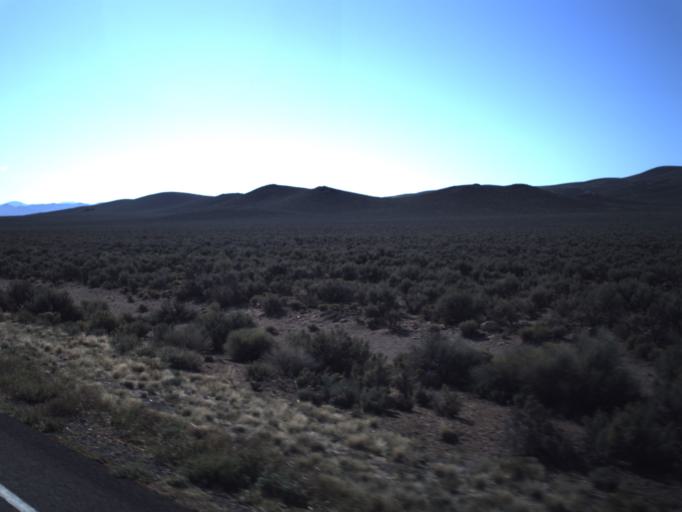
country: US
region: Utah
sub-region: Washington County
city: Enterprise
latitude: 37.7405
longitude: -113.7428
